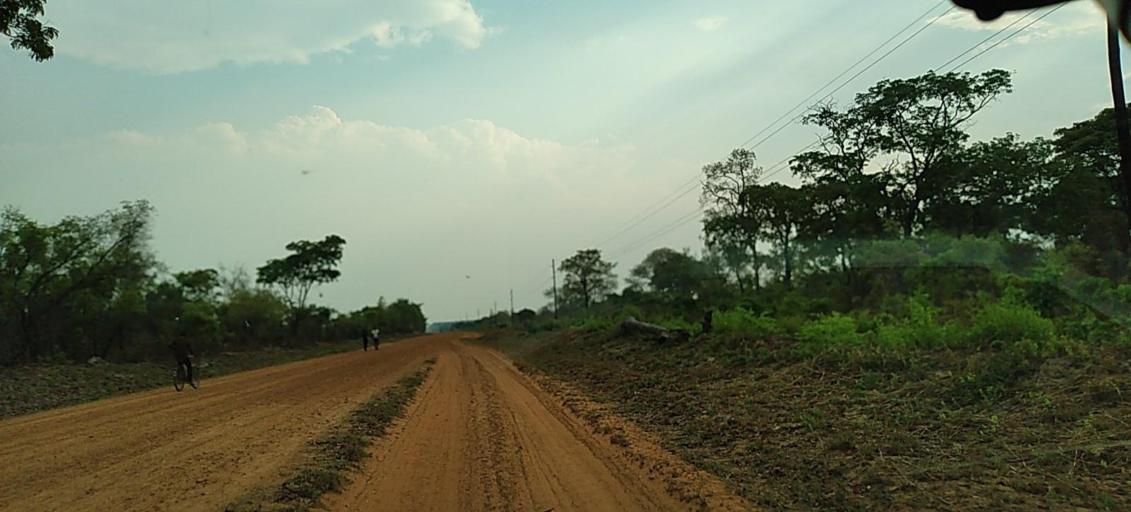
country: ZM
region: Western
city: Lukulu
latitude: -13.9039
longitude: 23.6543
